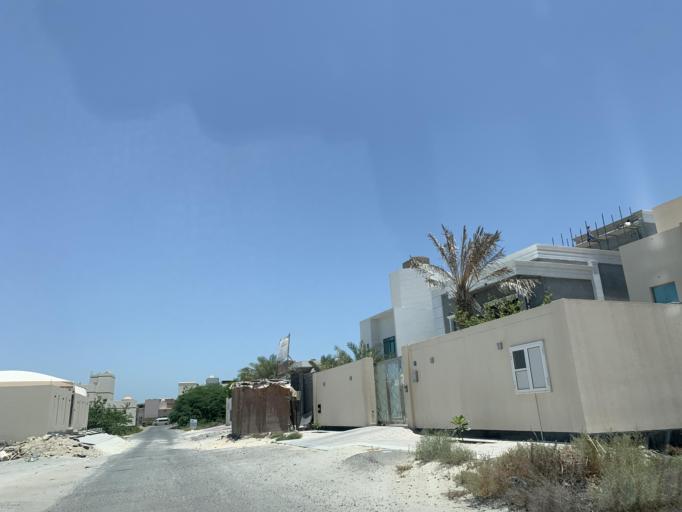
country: BH
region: Manama
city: Jidd Hafs
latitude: 26.2230
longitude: 50.4819
